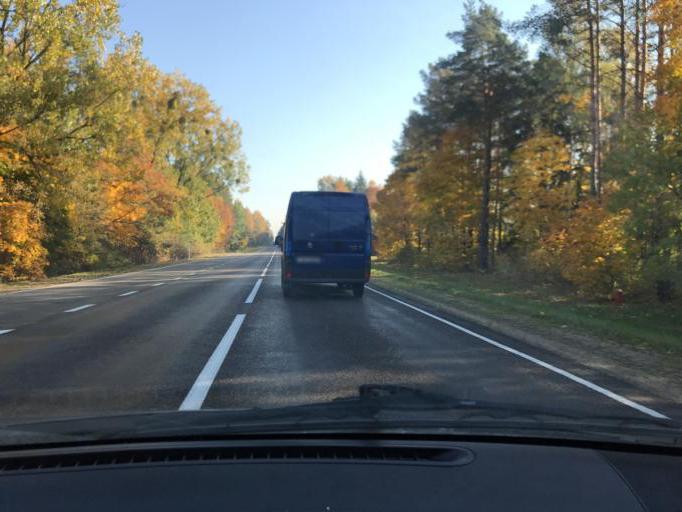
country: BY
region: Brest
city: Baranovichi
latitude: 52.9377
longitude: 26.0702
